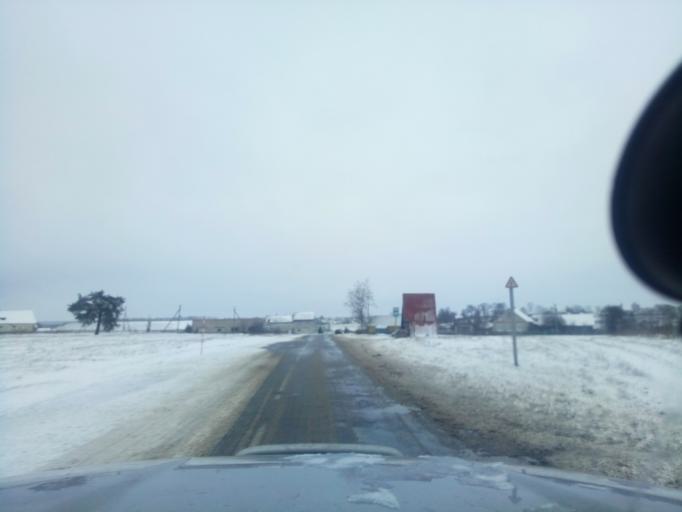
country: BY
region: Minsk
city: Tsimkavichy
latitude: 53.0654
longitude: 26.9758
